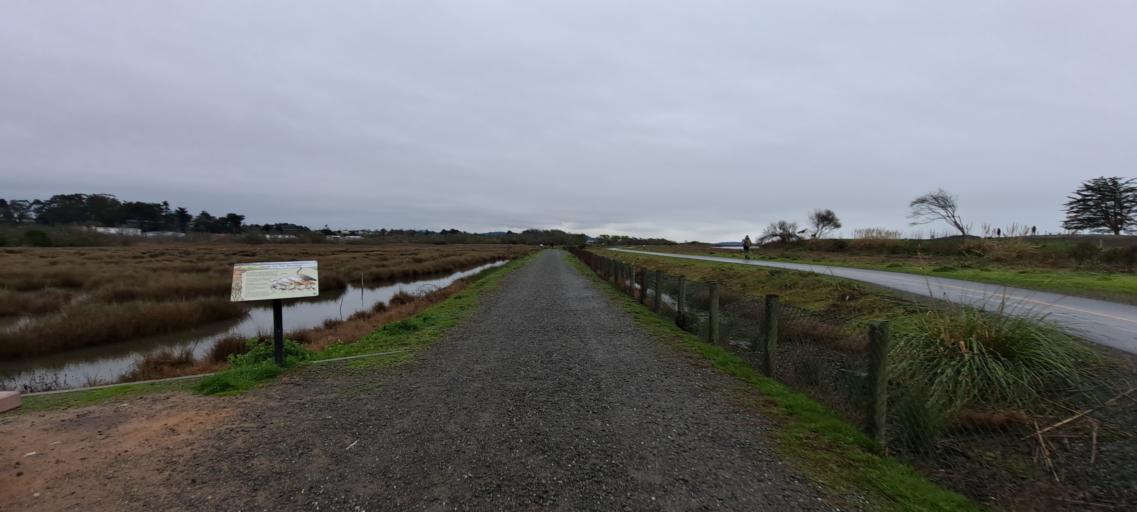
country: US
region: California
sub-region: Humboldt County
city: Bayview
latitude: 40.7894
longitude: -124.1856
